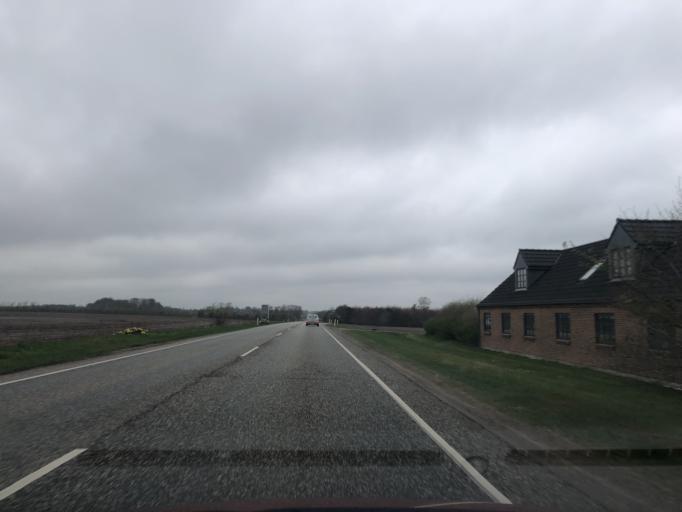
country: DK
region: Central Jutland
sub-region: Holstebro Kommune
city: Holstebro
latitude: 56.3105
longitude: 8.6965
